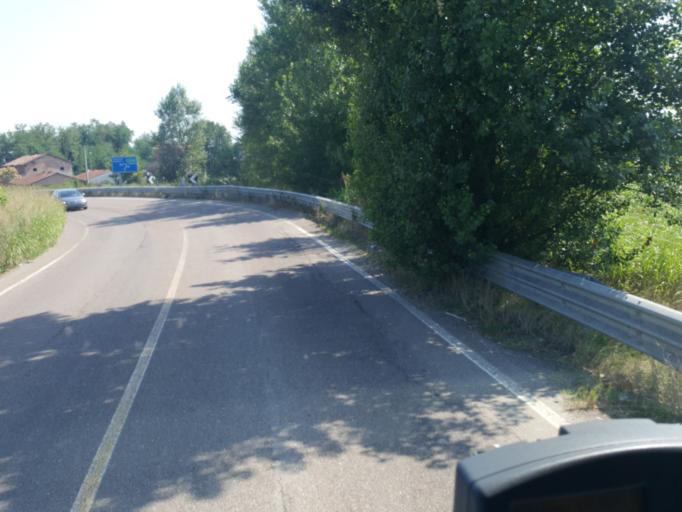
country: IT
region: Emilia-Romagna
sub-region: Provincia di Modena
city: San Vito
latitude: 44.5321
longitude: 10.9842
